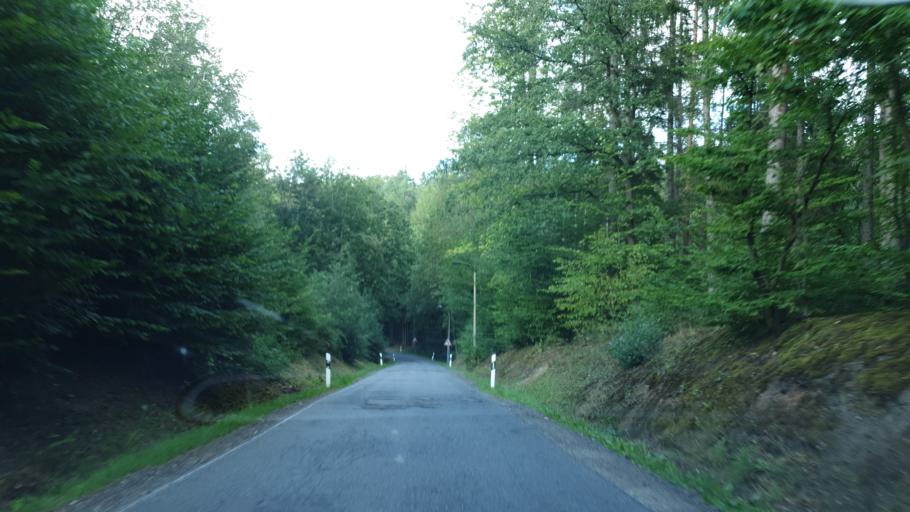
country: DE
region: Saxony
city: Lichtenstein
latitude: 50.7212
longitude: 12.6417
